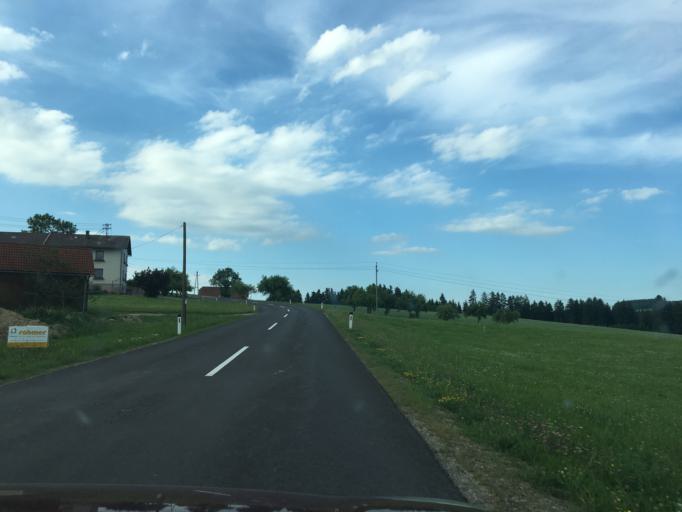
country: AT
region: Upper Austria
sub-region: Politischer Bezirk Urfahr-Umgebung
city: Reichenau im Muhlkreis
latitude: 48.4715
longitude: 14.3416
